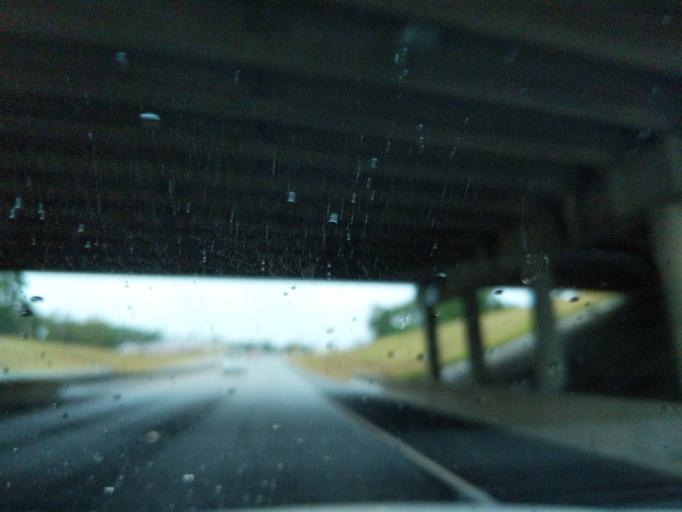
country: US
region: Texas
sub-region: Angelina County
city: Lufkin
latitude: 31.3155
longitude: -94.7105
